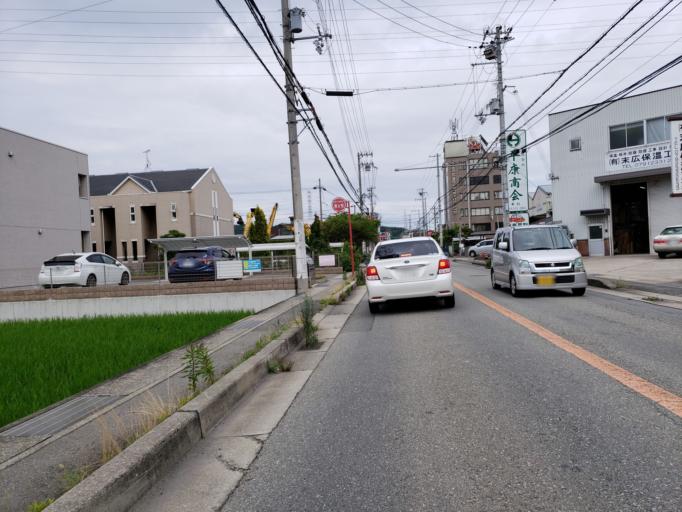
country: JP
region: Hyogo
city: Himeji
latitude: 34.7929
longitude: 134.6841
